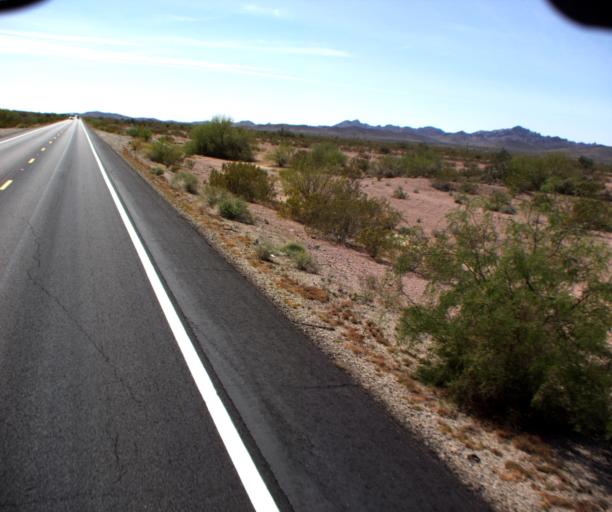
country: US
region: Arizona
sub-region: La Paz County
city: Quartzsite
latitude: 33.3014
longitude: -114.2195
